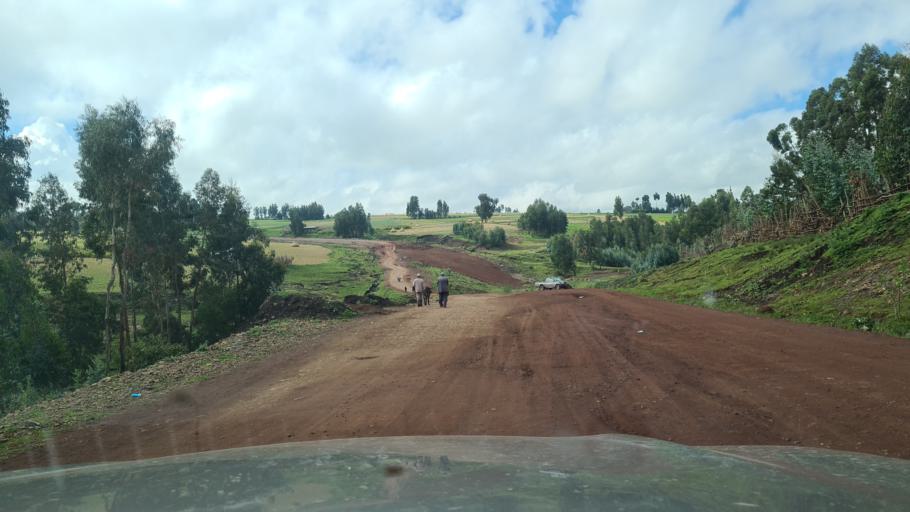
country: ET
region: Oromiya
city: Huruta
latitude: 8.1276
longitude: 39.4355
